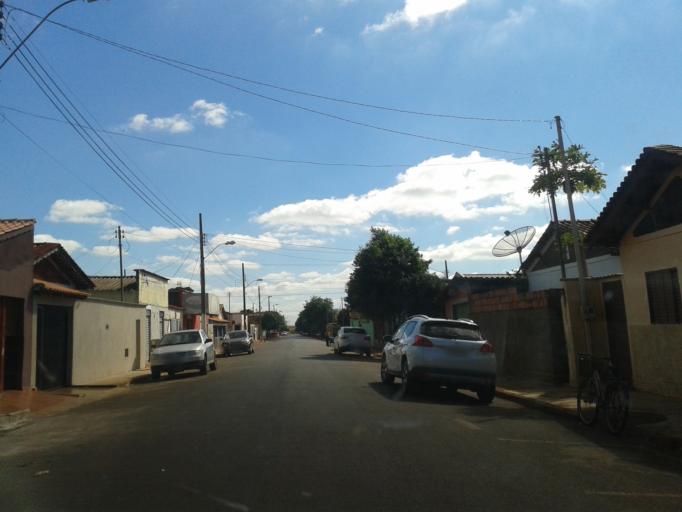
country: BR
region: Minas Gerais
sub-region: Centralina
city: Centralina
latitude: -18.5859
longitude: -49.2022
